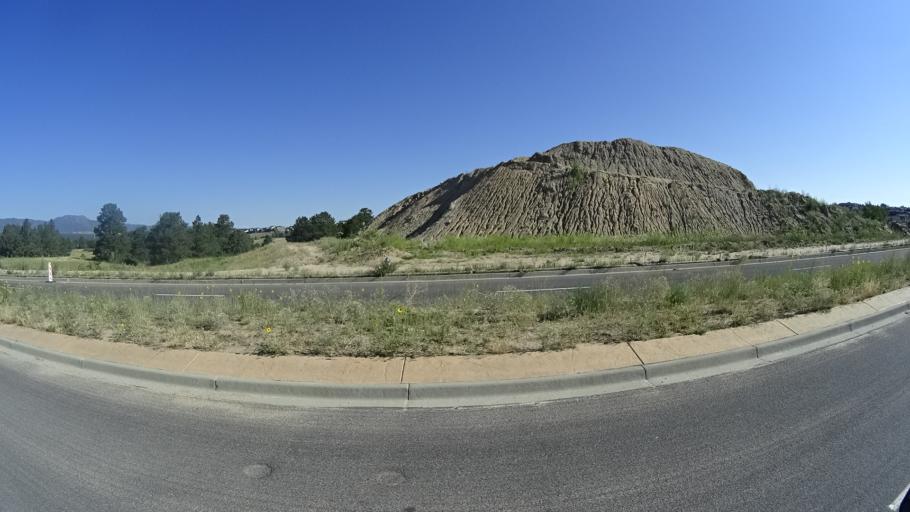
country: US
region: Colorado
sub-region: El Paso County
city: Gleneagle
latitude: 38.9976
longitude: -104.8073
